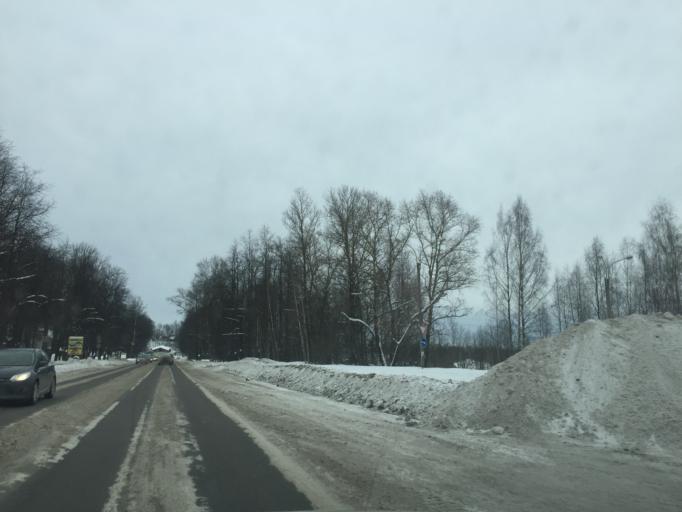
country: RU
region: Leningrad
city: Yanino Vtoroye
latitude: 59.9418
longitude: 30.6069
